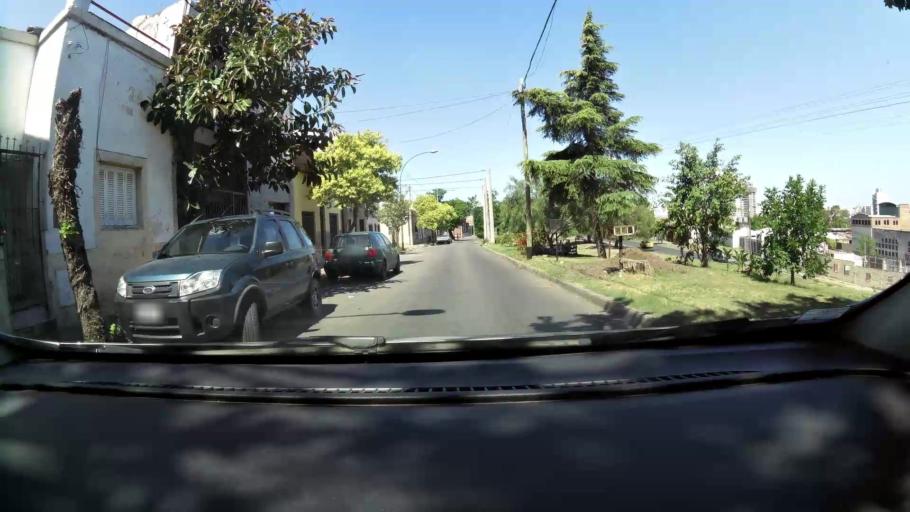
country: AR
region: Cordoba
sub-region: Departamento de Capital
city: Cordoba
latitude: -31.4041
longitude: -64.1800
